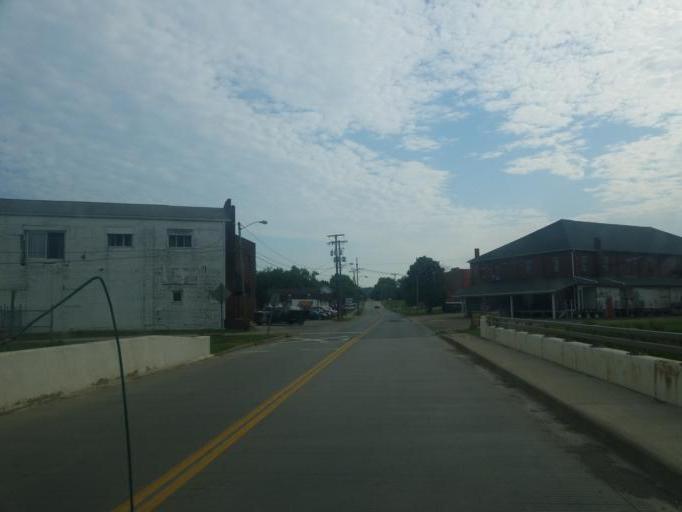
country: US
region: Ohio
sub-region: Wayne County
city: Wooster
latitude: 40.7883
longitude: -81.9413
